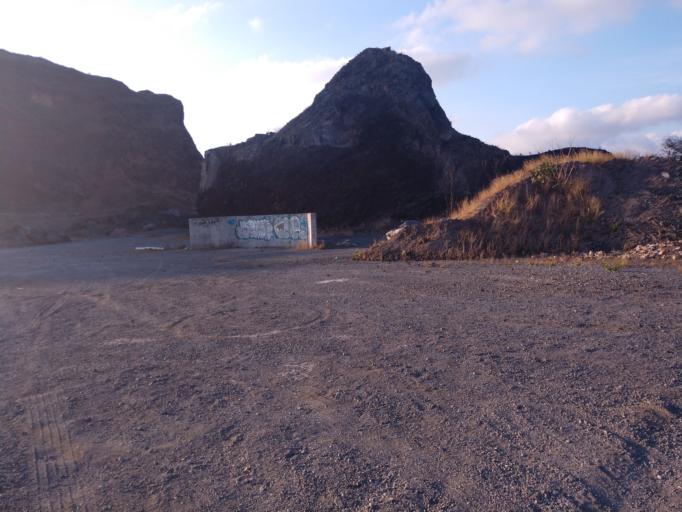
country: MX
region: Nayarit
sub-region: Tepic
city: La Corregidora
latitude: 21.4759
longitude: -104.8118
